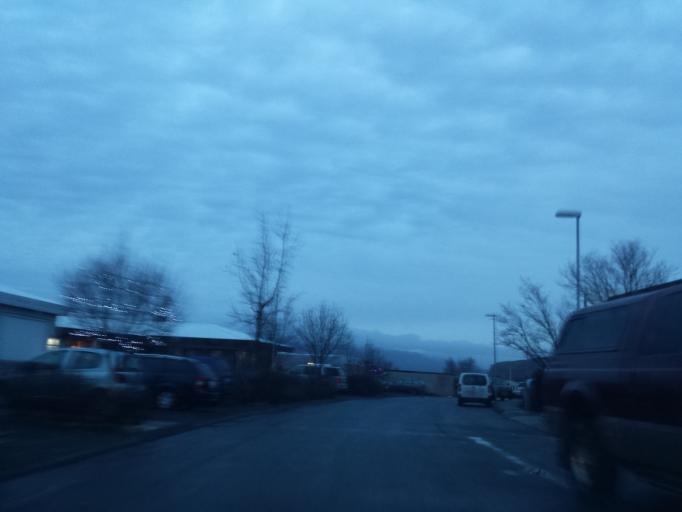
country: IS
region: Capital Region
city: Mosfellsbaer
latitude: 64.1370
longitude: -21.7771
